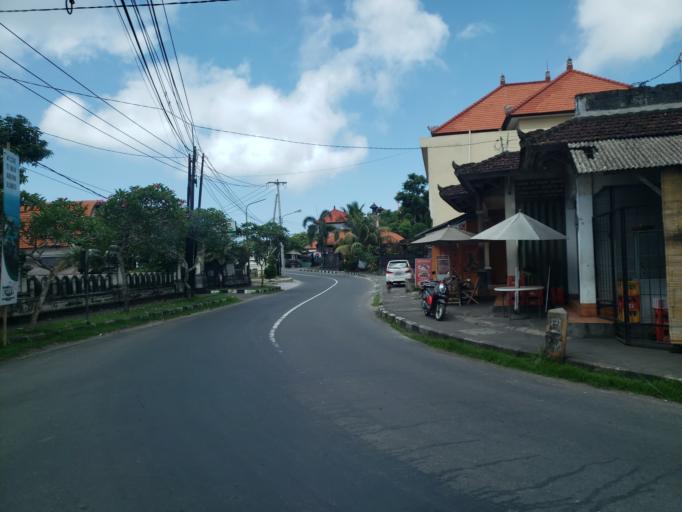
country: ID
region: Bali
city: Kangin
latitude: -8.8340
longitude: 115.1261
